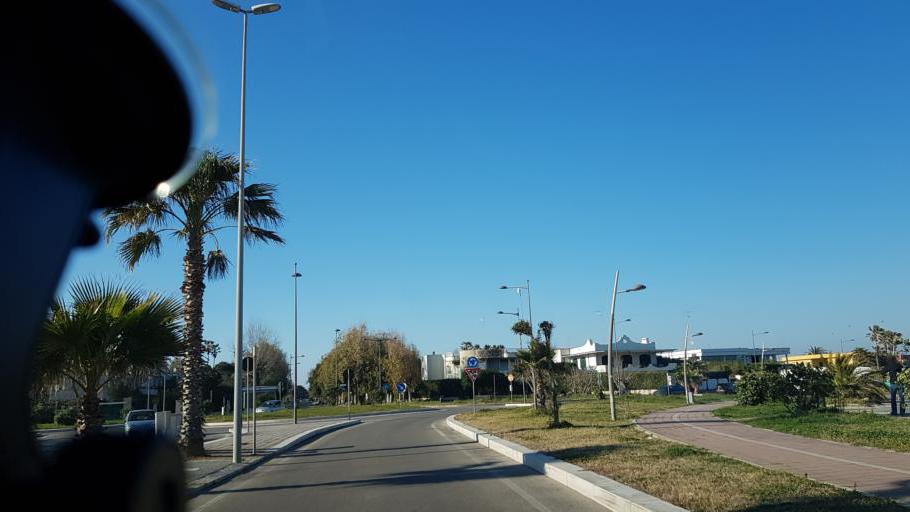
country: IT
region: Apulia
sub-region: Provincia di Lecce
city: Struda
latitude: 40.3871
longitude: 18.3041
